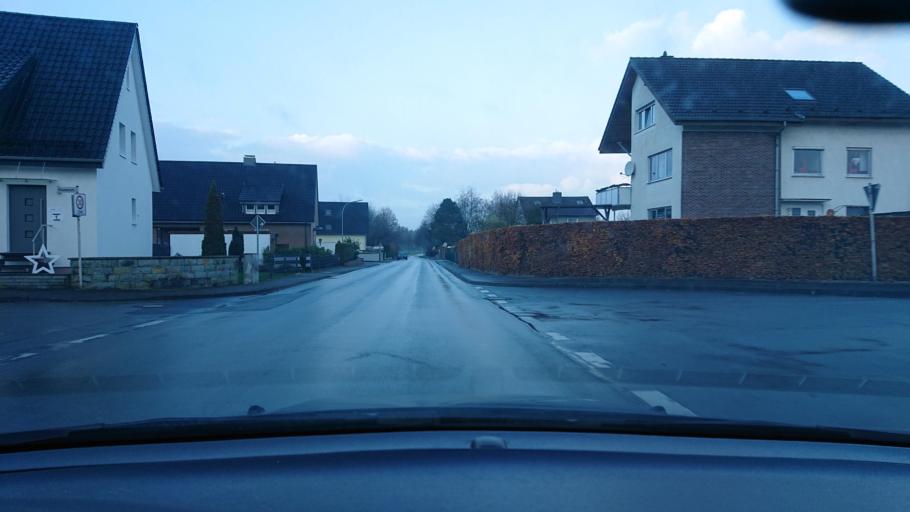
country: DE
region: North Rhine-Westphalia
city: Erwitte
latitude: 51.6162
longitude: 8.3293
